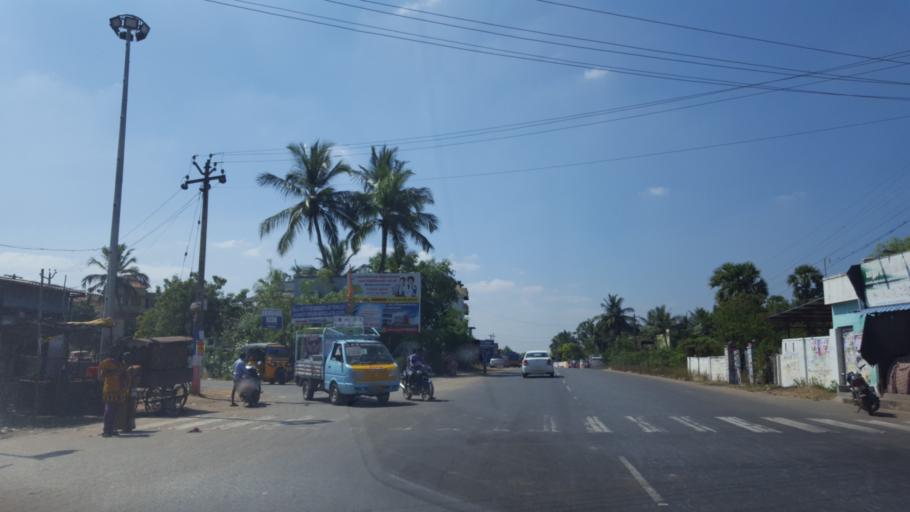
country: IN
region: Tamil Nadu
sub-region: Kancheepuram
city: Karumbakkam
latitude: 12.7151
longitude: 80.1876
